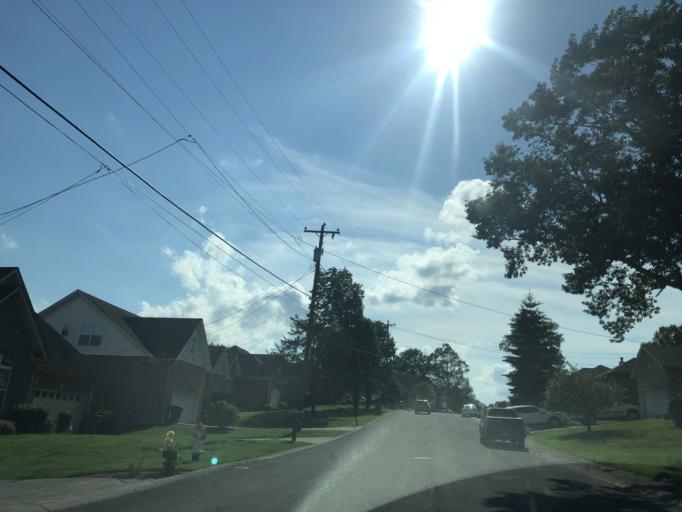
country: US
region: Tennessee
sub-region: Davidson County
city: Nashville
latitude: 36.2278
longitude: -86.8005
